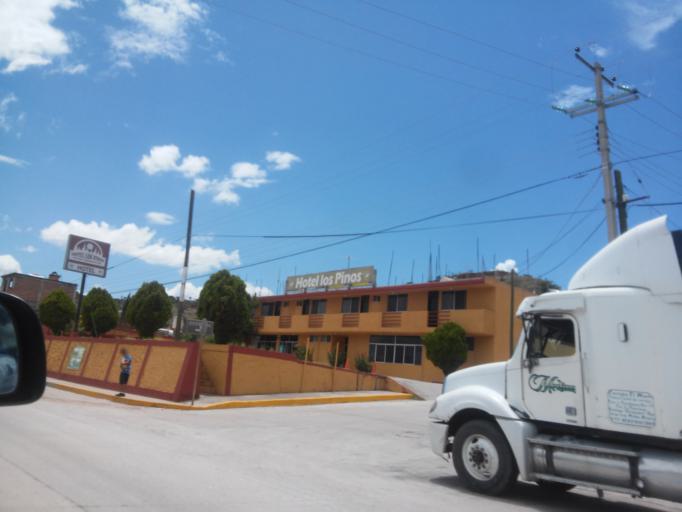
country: MX
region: Durango
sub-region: Santiago Papasquiaro
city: Santiago Papasquiaro
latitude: 25.0539
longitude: -105.4246
